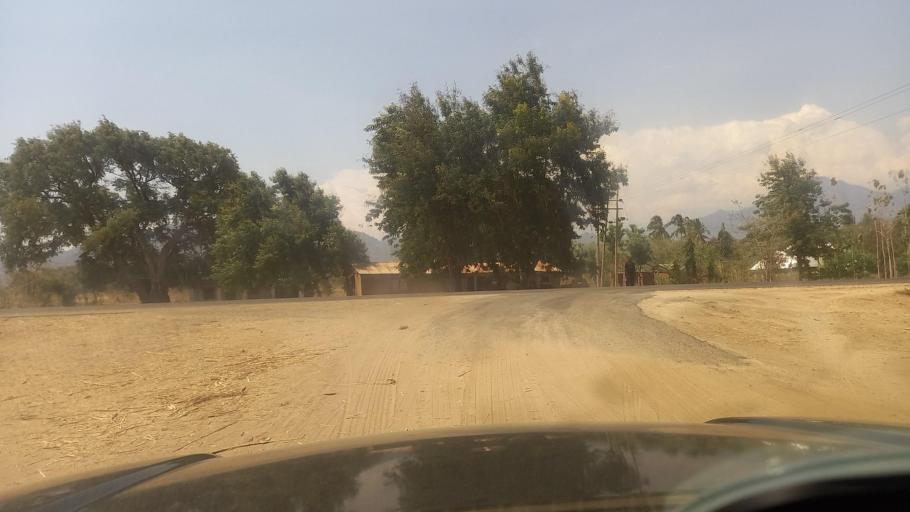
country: TZ
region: Morogoro
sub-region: Mvomero District
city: Mvomero
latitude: -6.3298
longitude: 37.4267
